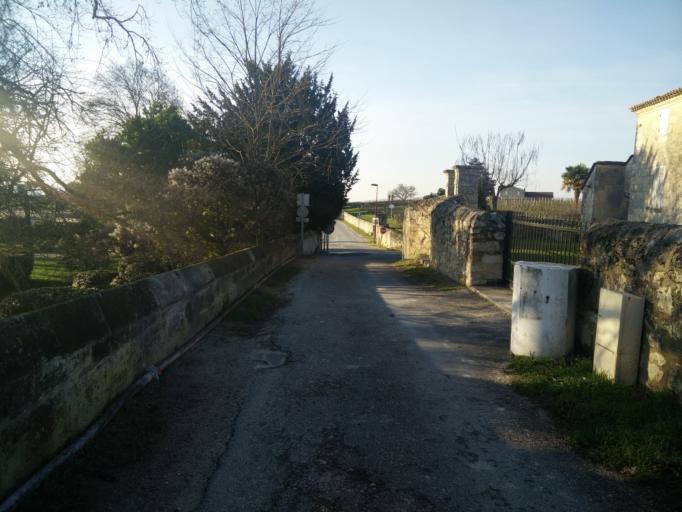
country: FR
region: Aquitaine
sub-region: Departement de la Gironde
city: Saint-Emilion
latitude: 44.8887
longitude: -0.1611
